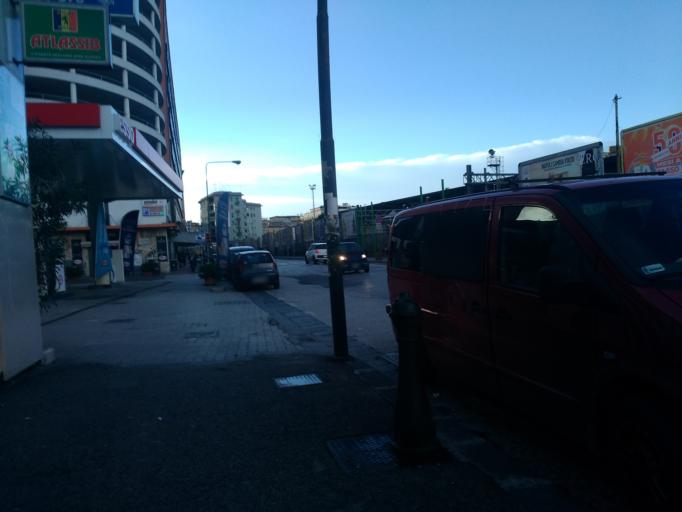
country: IT
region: Campania
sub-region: Provincia di Napoli
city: Napoli
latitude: 40.8504
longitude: 14.2763
